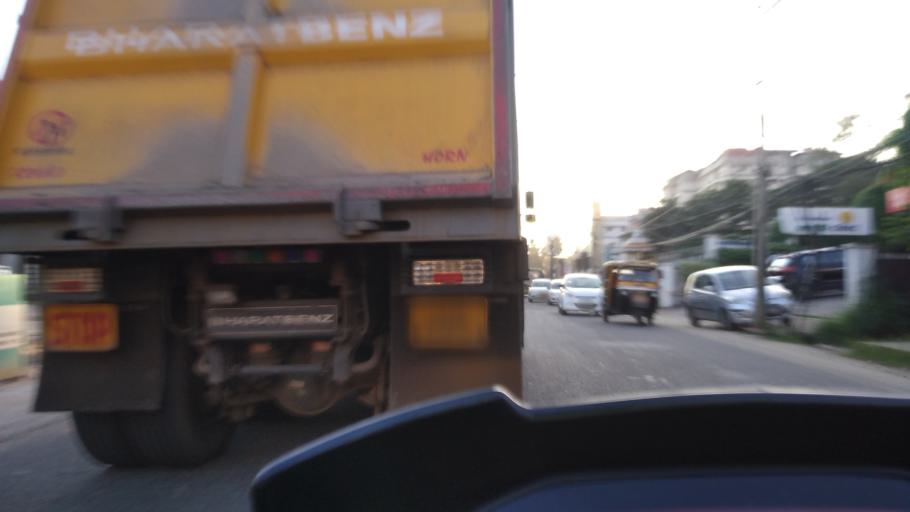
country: IN
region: Kerala
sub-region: Ernakulam
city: Cochin
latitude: 9.9537
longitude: 76.3428
